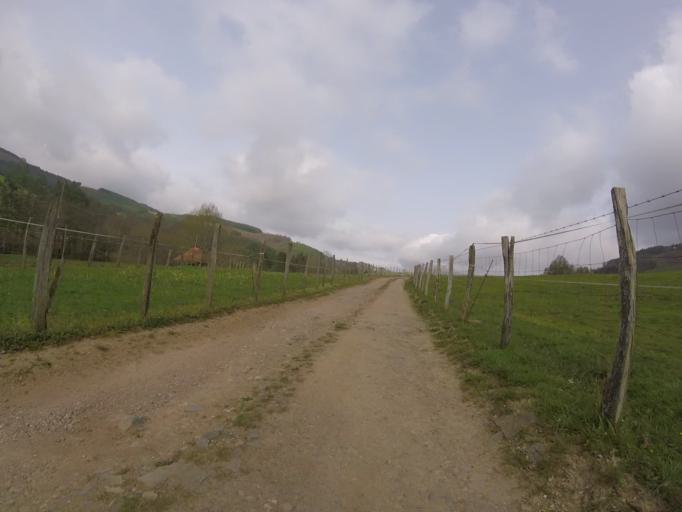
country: ES
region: Navarre
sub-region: Provincia de Navarra
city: Areso
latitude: 43.1077
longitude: -1.9570
